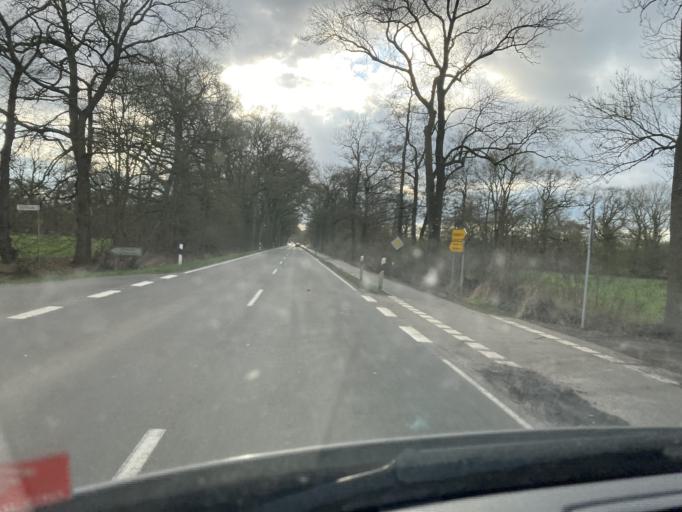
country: DE
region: Lower Saxony
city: Ostrhauderfehn
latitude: 53.1624
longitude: 7.5603
